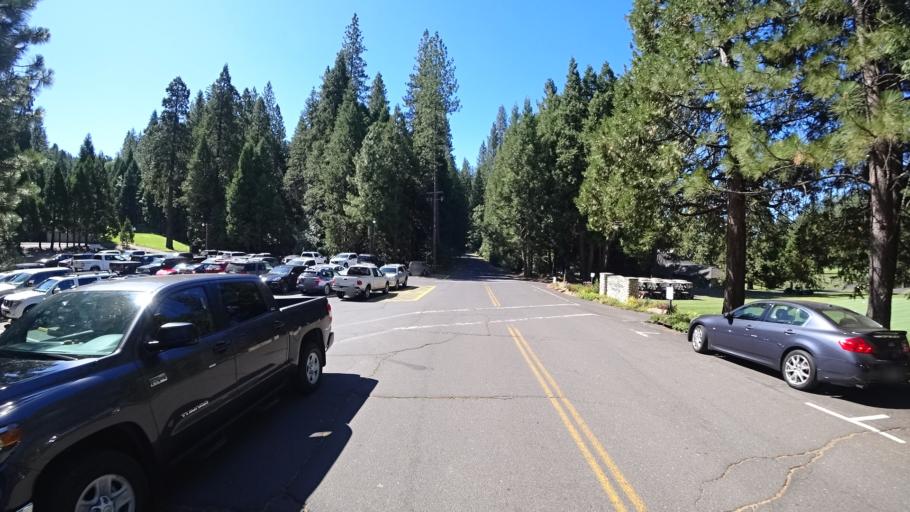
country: US
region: California
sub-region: Calaveras County
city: Arnold
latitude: 38.2564
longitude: -120.3276
